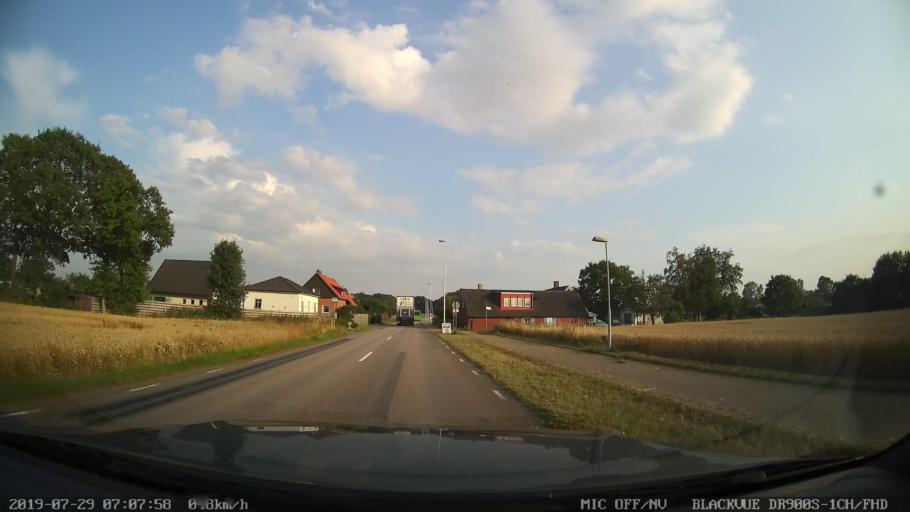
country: SE
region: Skane
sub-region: Helsingborg
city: Odakra
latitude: 56.1033
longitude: 12.6963
